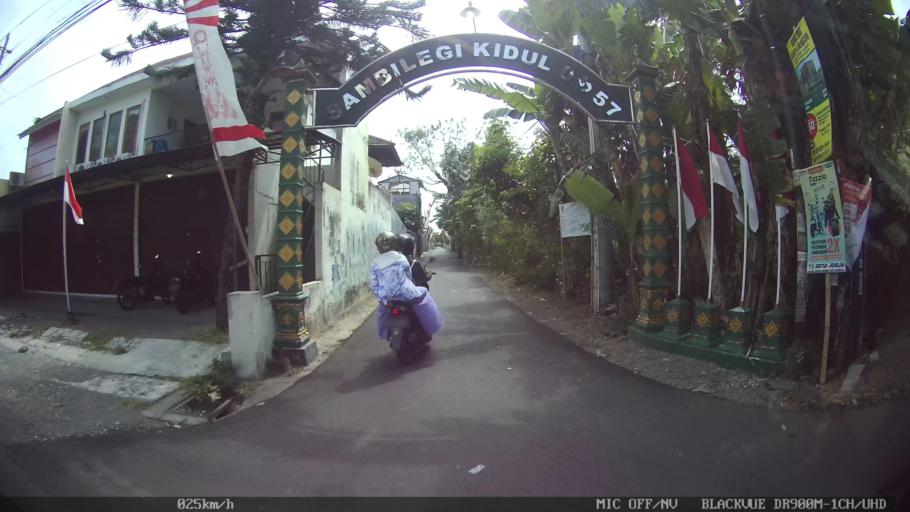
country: ID
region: Daerah Istimewa Yogyakarta
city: Depok
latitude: -7.7812
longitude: 110.4345
